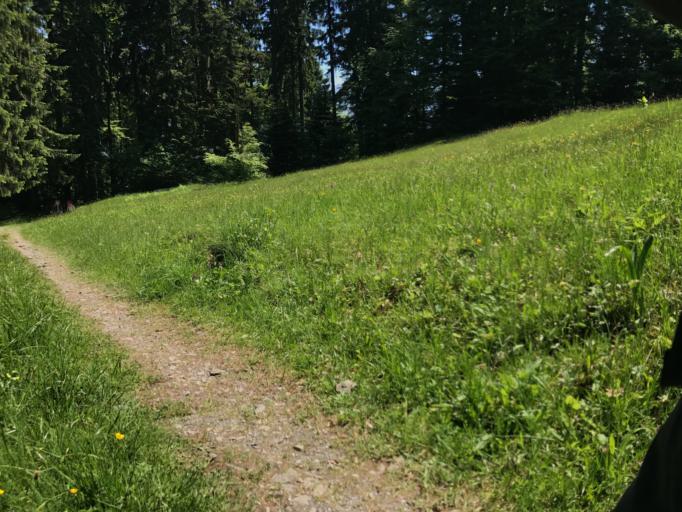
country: CH
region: Nidwalden
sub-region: Nidwalden
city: Hergiswil
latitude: 46.9947
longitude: 8.2921
